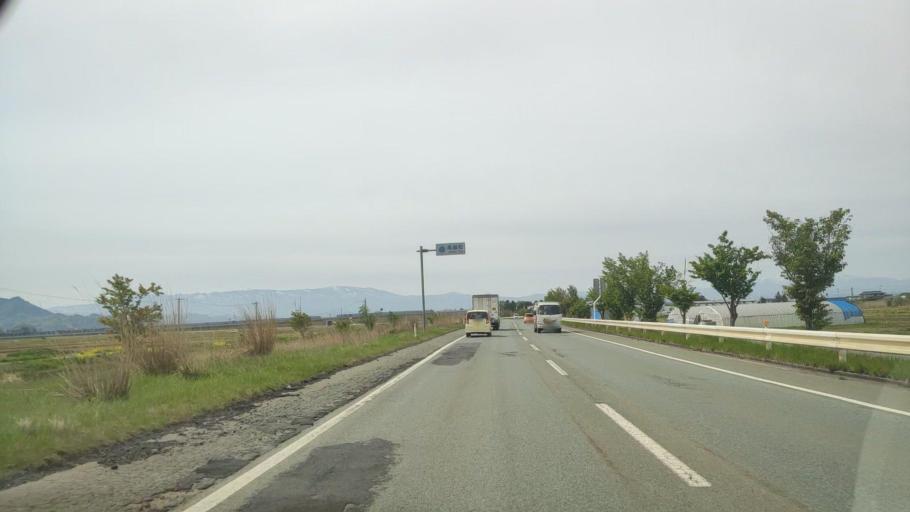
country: JP
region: Yamagata
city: Takahata
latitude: 38.0352
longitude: 140.1727
